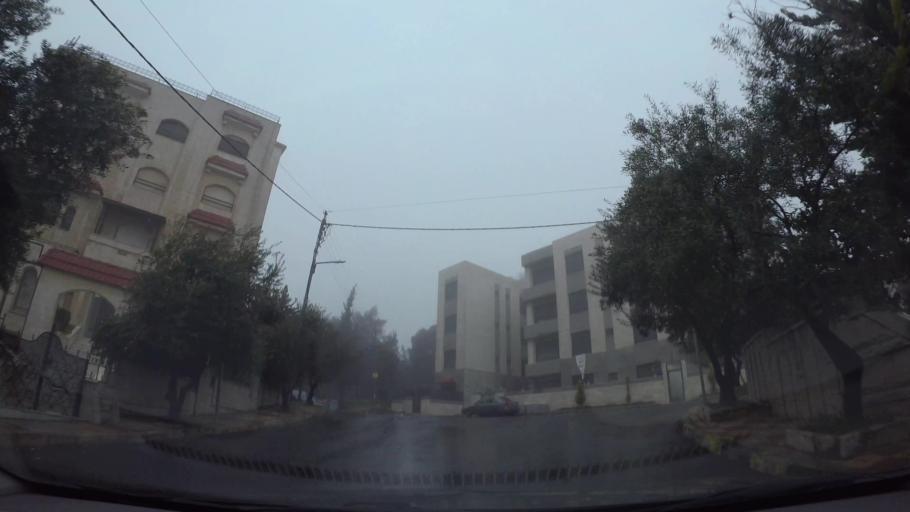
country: JO
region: Amman
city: Al Jubayhah
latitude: 32.0206
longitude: 35.8801
